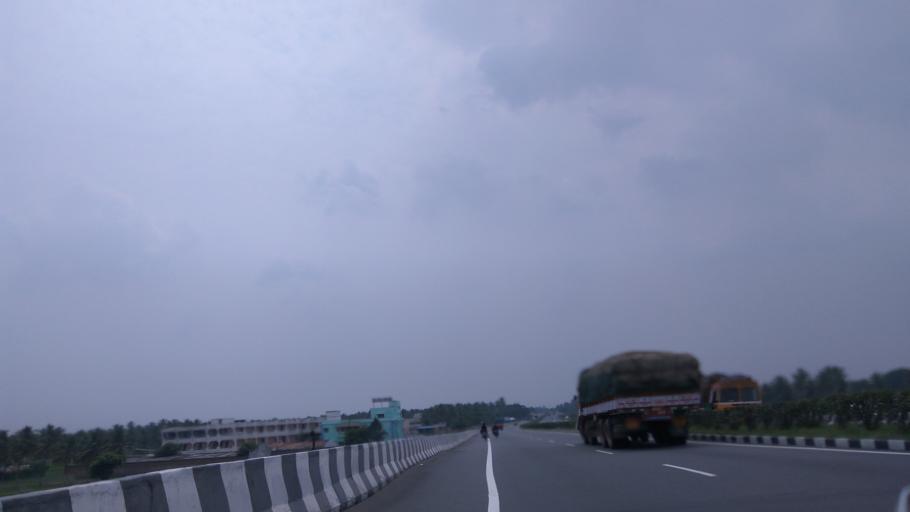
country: IN
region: Tamil Nadu
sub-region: Dharmapuri
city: Dharmapuri
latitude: 12.2437
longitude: 78.1951
